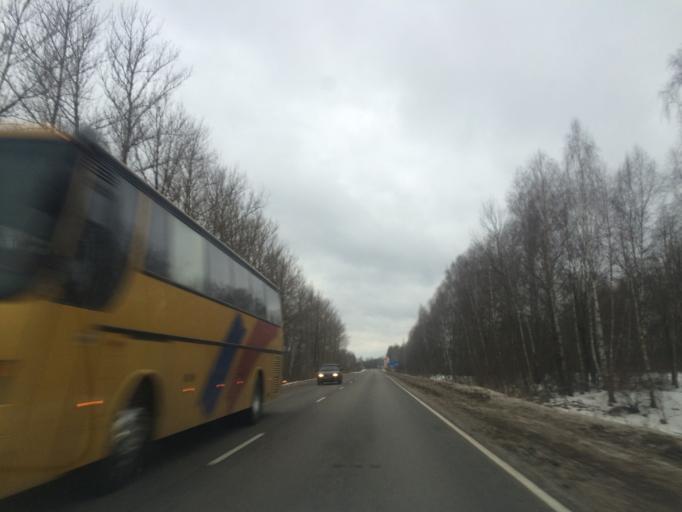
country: RU
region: Tula
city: Leninskiy
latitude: 54.1344
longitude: 37.2888
